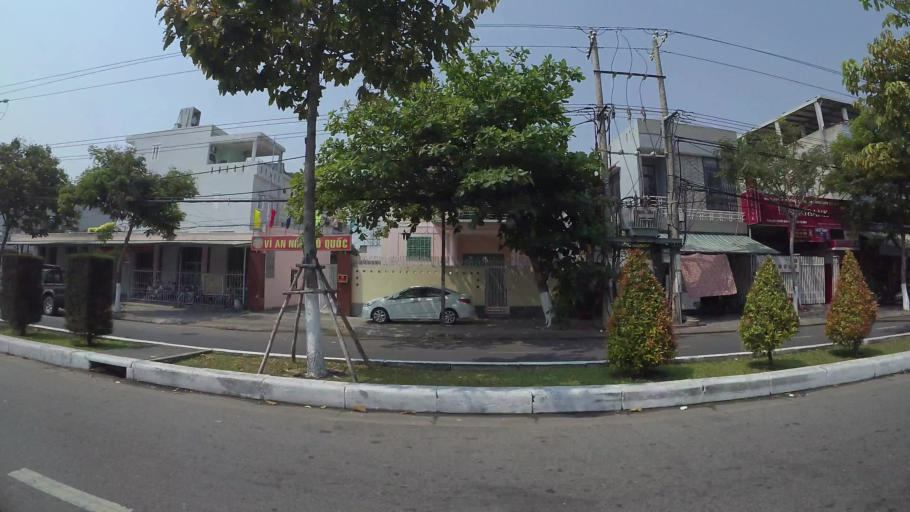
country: VN
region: Da Nang
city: Son Tra
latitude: 16.0408
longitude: 108.2416
